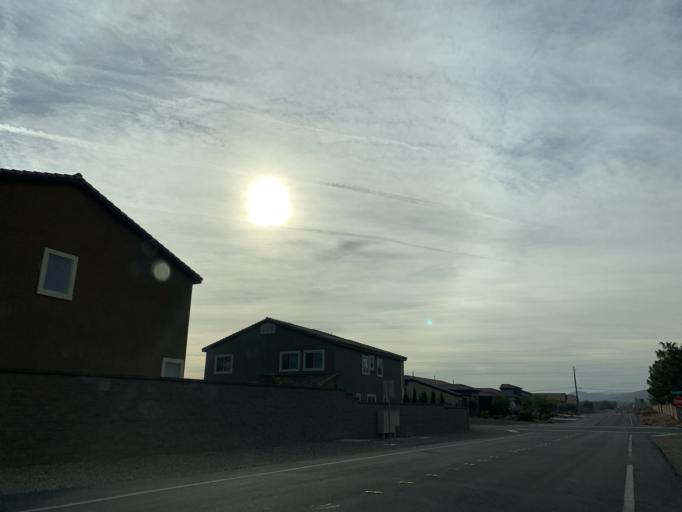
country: US
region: Nevada
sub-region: Clark County
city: Enterprise
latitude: 36.0051
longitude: -115.1856
